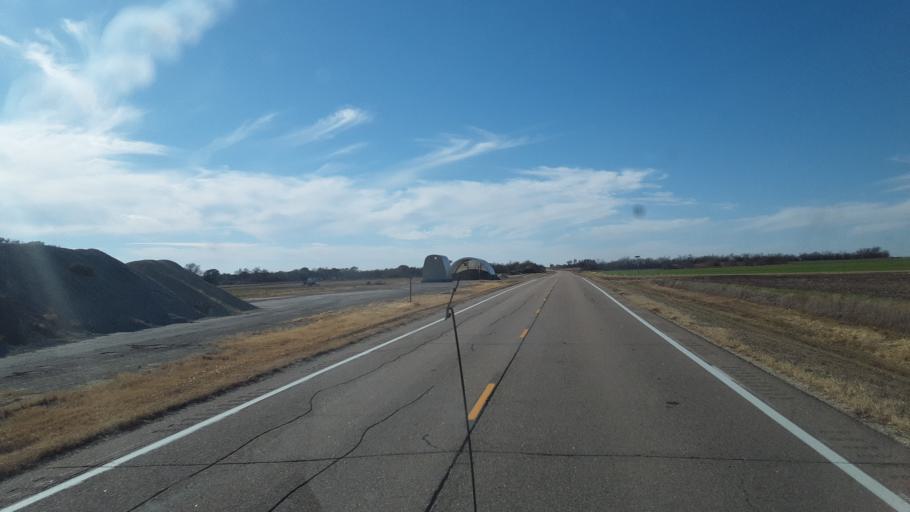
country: US
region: Kansas
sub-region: Pawnee County
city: Larned
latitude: 38.1895
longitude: -99.2935
